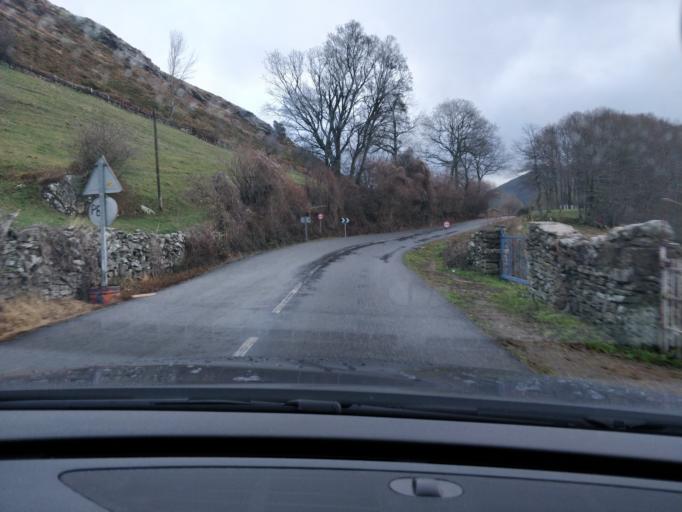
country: ES
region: Castille and Leon
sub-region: Provincia de Burgos
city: Espinosa de los Monteros
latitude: 43.1042
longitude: -3.5721
